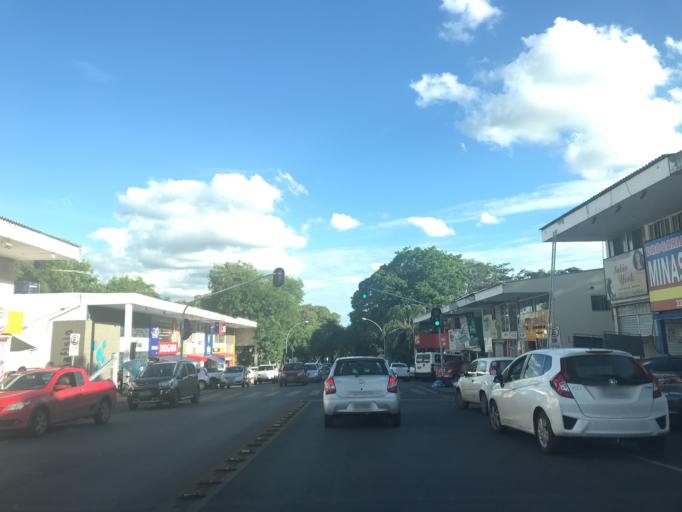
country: BR
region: Federal District
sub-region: Brasilia
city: Brasilia
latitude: -15.8307
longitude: -47.9160
